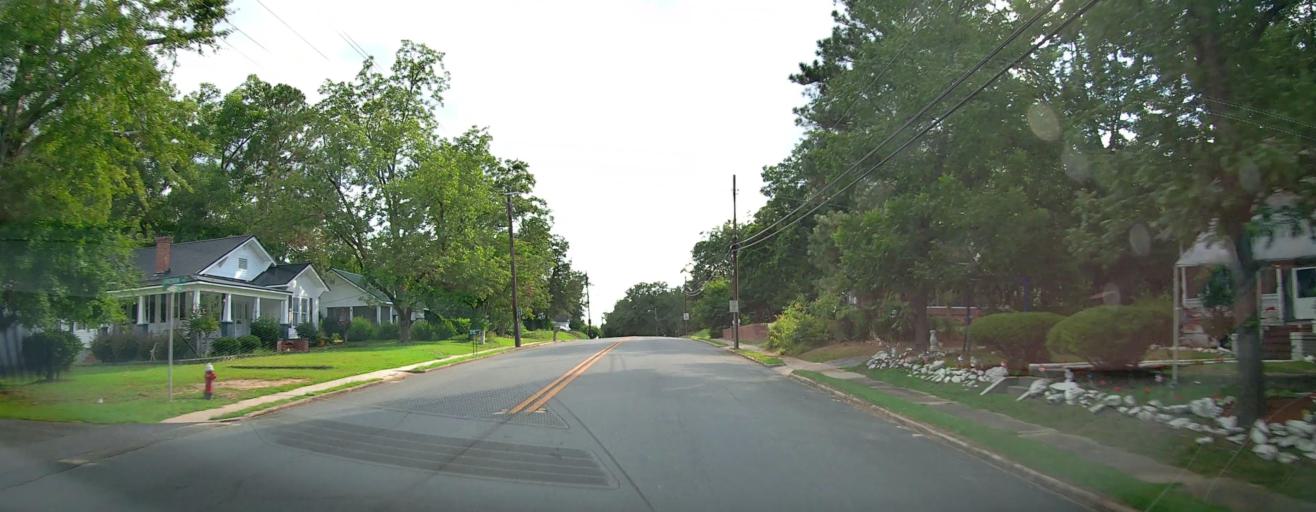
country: US
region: Georgia
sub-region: Crawford County
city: Roberta
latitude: 32.7176
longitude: -84.0144
